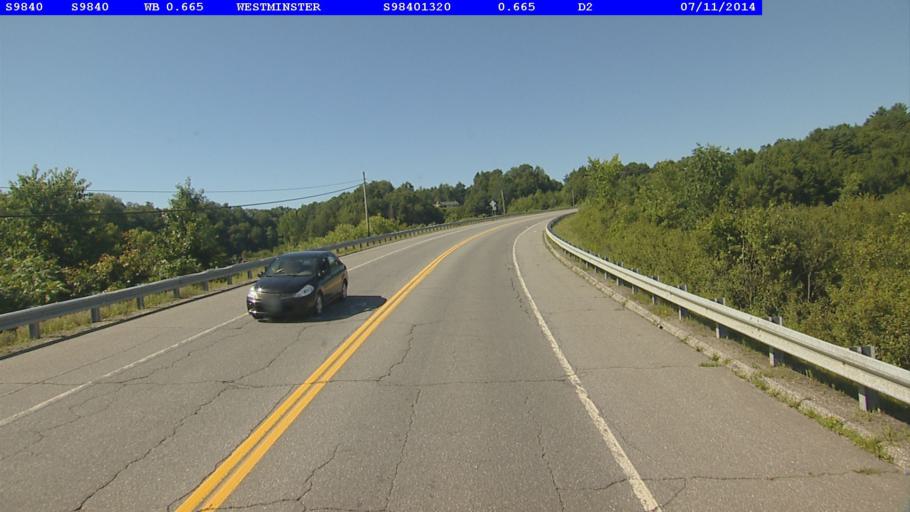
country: US
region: Vermont
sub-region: Windham County
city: Bellows Falls
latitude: 43.0934
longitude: -72.4452
